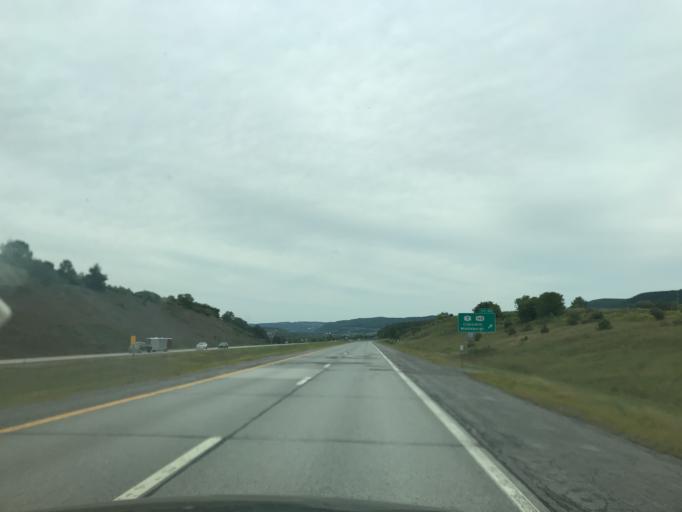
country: US
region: New York
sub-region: Schoharie County
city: Cobleskill
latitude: 42.6768
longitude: -74.4277
